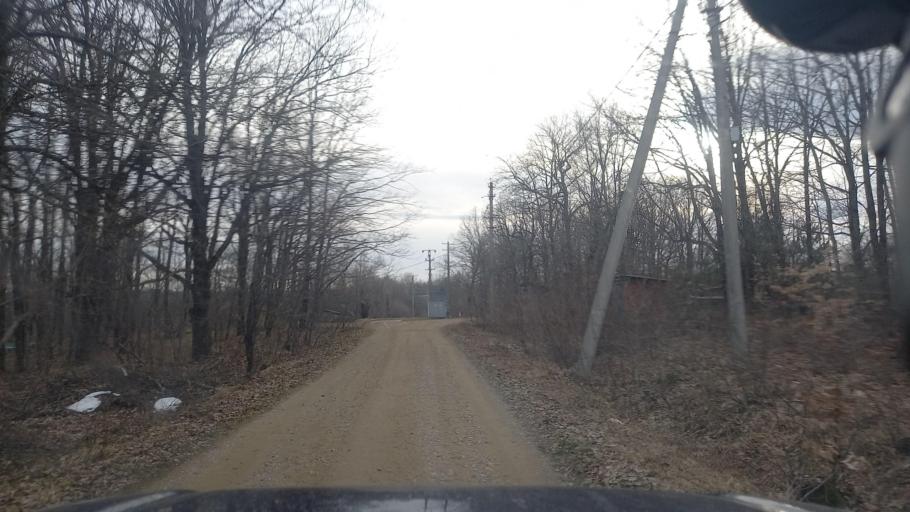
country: RU
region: Krasnodarskiy
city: Goryachiy Klyuch
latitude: 44.6960
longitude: 39.0203
